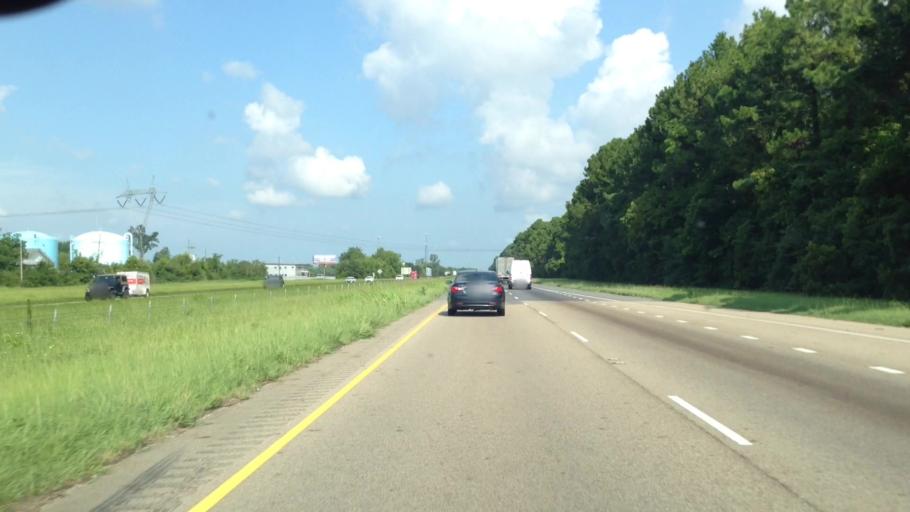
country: US
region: Louisiana
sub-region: Saint John the Baptist Parish
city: Laplace
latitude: 30.0906
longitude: -90.4487
